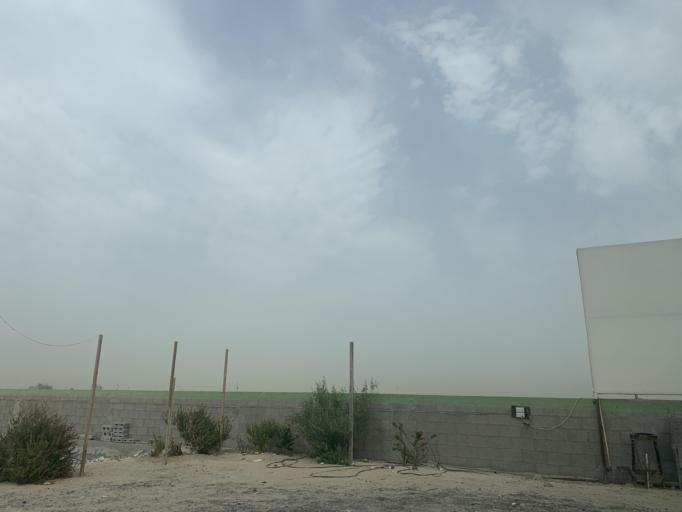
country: BH
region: Northern
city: Madinat `Isa
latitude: 26.1803
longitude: 50.5086
